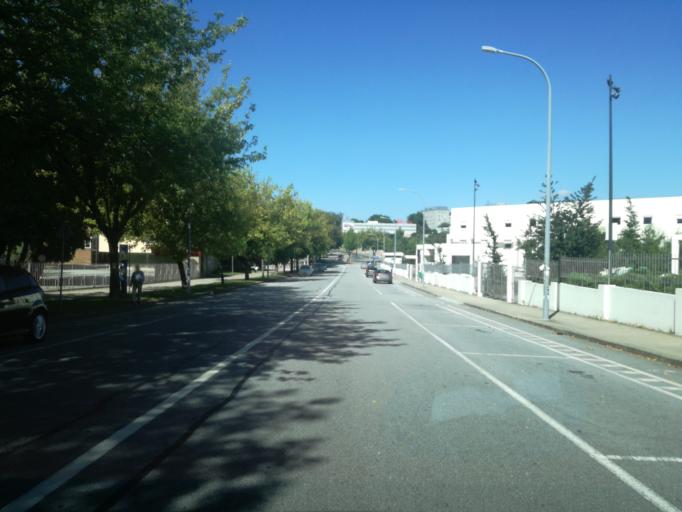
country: PT
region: Porto
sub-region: Matosinhos
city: Sao Mamede de Infesta
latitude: 41.1772
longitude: -8.6075
